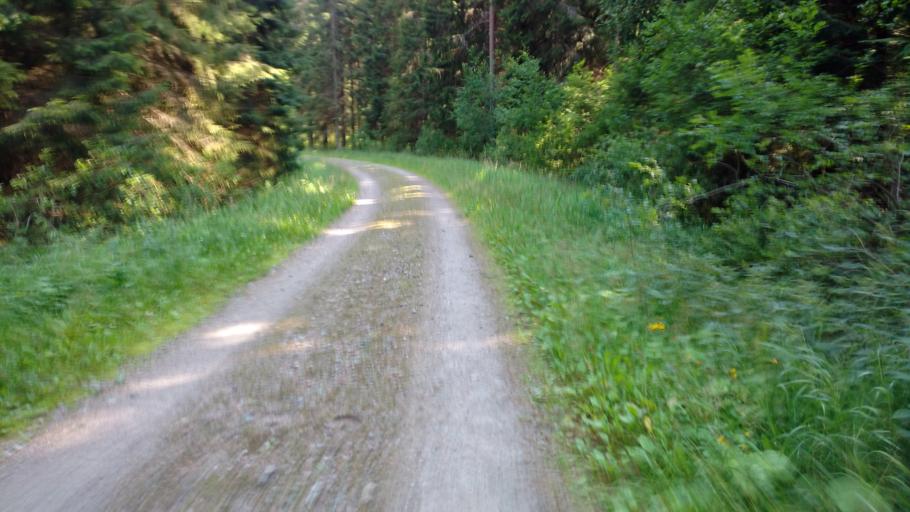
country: FI
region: Varsinais-Suomi
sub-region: Salo
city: Pertteli
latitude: 60.4013
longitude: 23.2150
